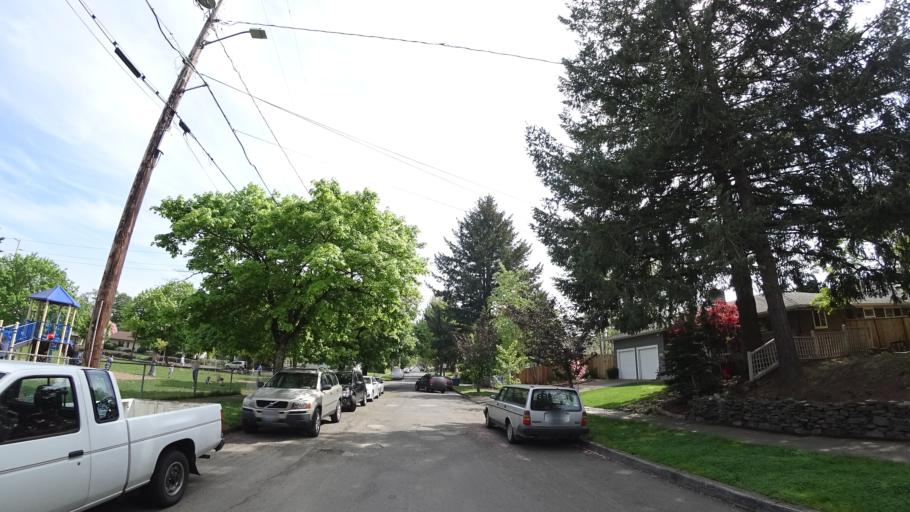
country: US
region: Oregon
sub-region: Clackamas County
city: Milwaukie
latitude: 45.4819
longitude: -122.6134
